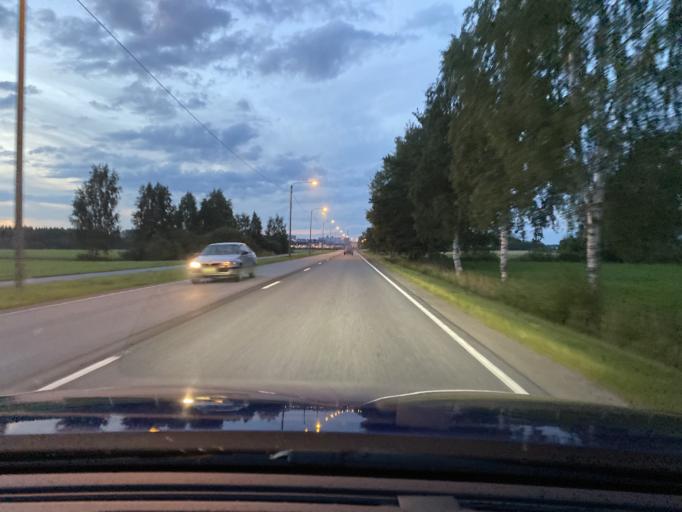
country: FI
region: Southern Ostrobothnia
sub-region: Suupohja
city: Kauhajoki
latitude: 62.4395
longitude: 22.2087
